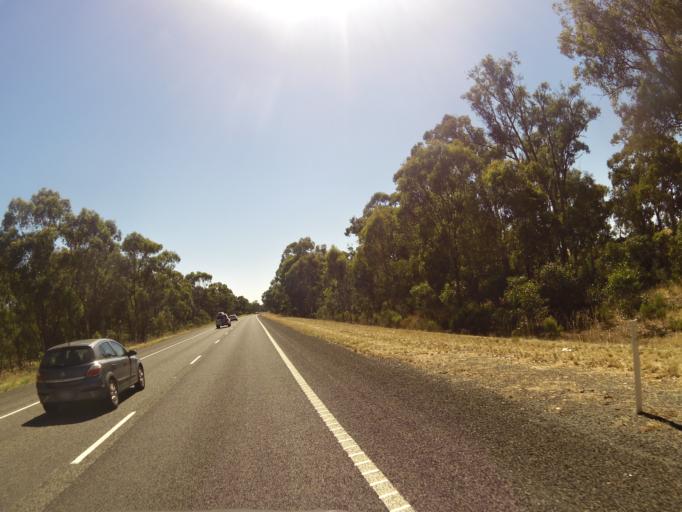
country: AU
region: Victoria
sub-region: Greater Shepparton
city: Shepparton
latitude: -36.8651
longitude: 145.2978
